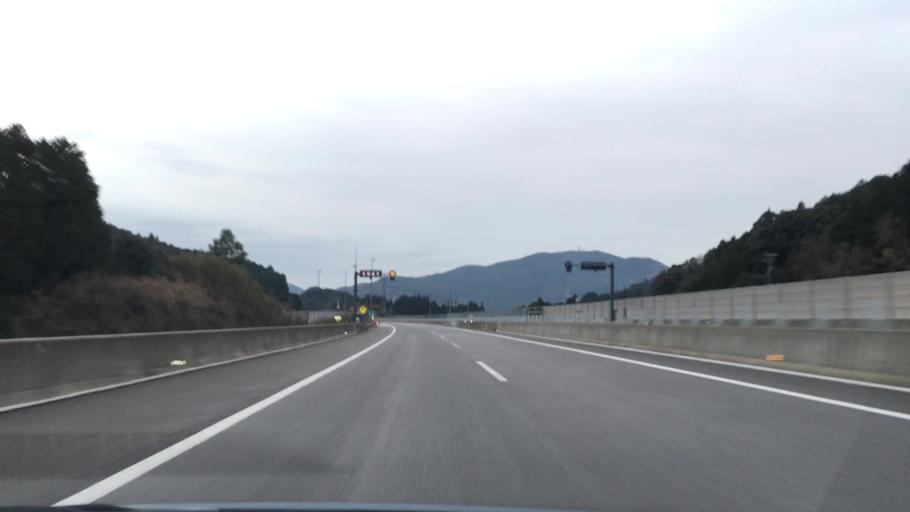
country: JP
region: Aichi
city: Shinshiro
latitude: 34.8743
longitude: 137.6441
